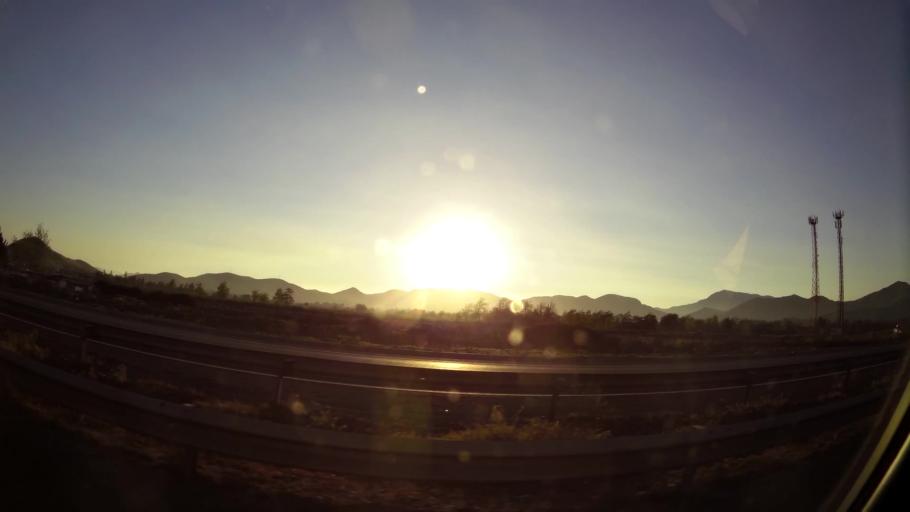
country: CL
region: Santiago Metropolitan
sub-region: Provincia de Santiago
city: Lo Prado
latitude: -33.5177
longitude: -70.7992
